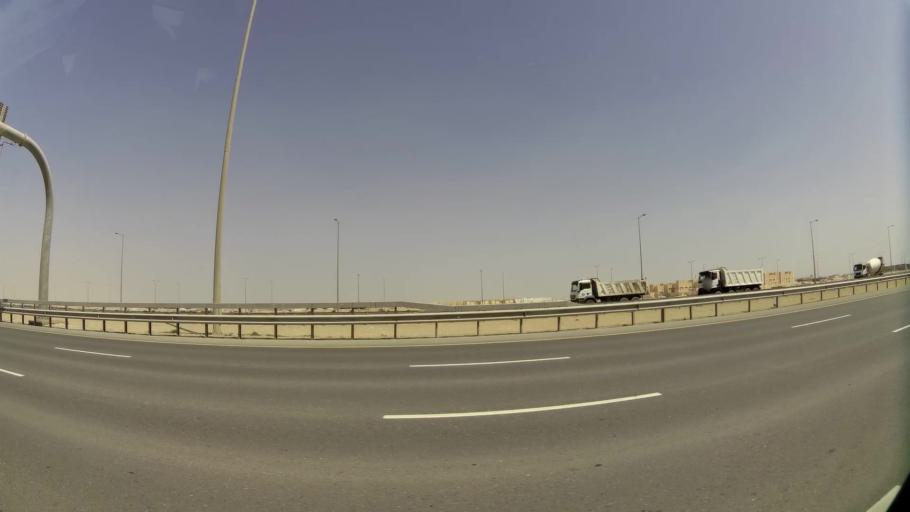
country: QA
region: Baladiyat Umm Salal
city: Umm Salal Muhammad
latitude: 25.4187
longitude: 51.4204
